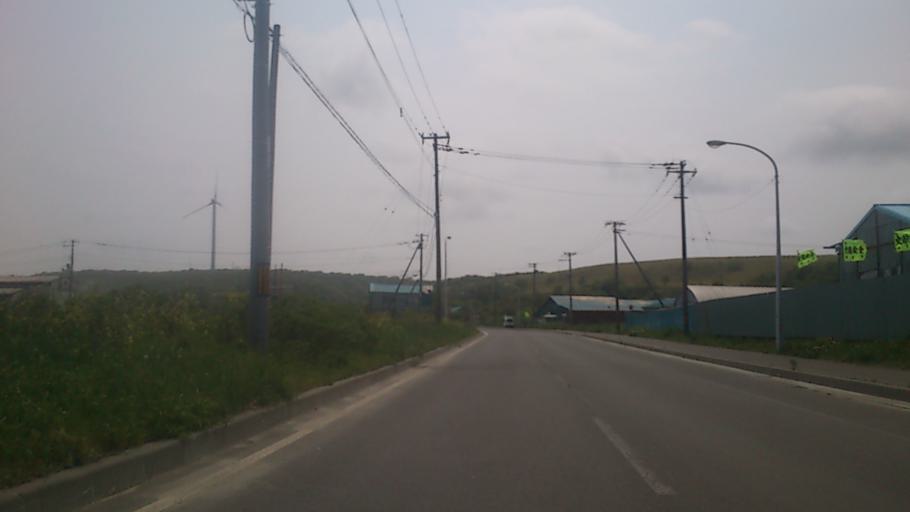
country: JP
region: Hokkaido
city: Nemuro
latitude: 43.2835
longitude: 145.5667
